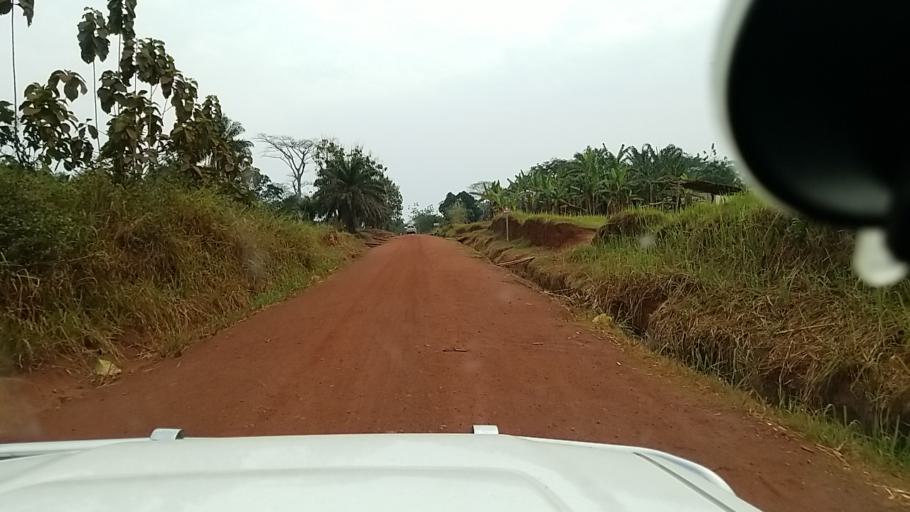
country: CD
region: Equateur
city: Gemena
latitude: 2.9693
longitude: 19.9001
